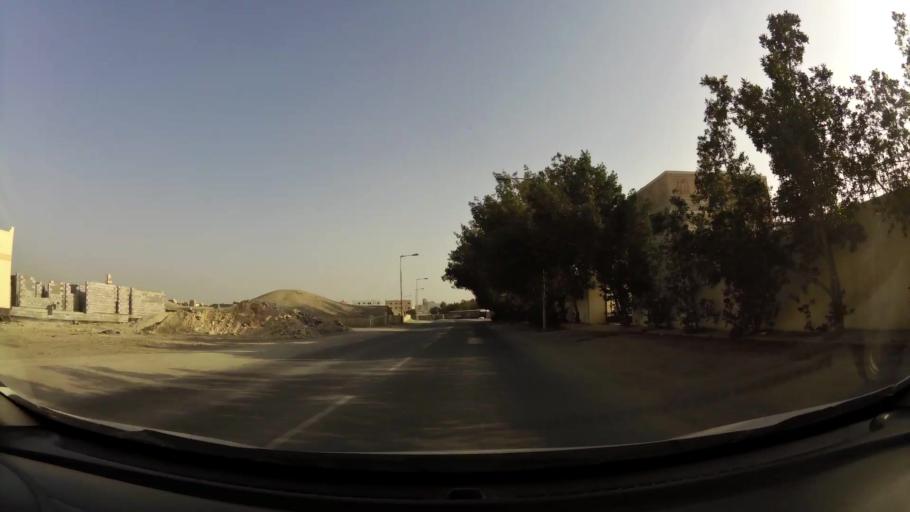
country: BH
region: Manama
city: Jidd Hafs
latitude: 26.2144
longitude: 50.5000
